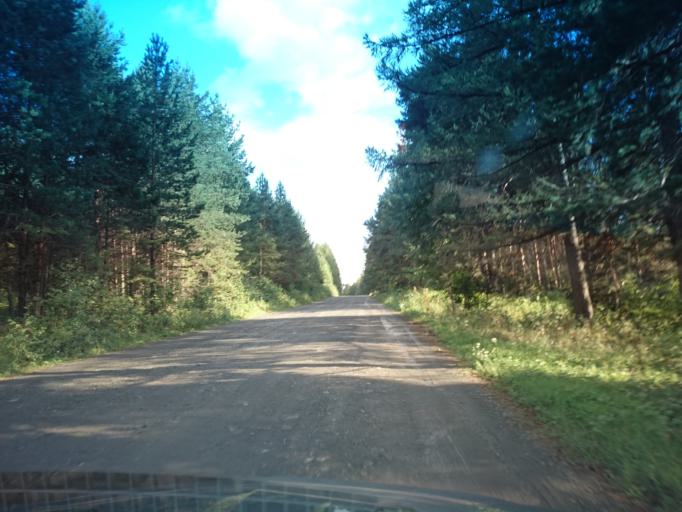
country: RU
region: Bashkortostan
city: Beloretsk
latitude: 54.0426
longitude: 58.3306
